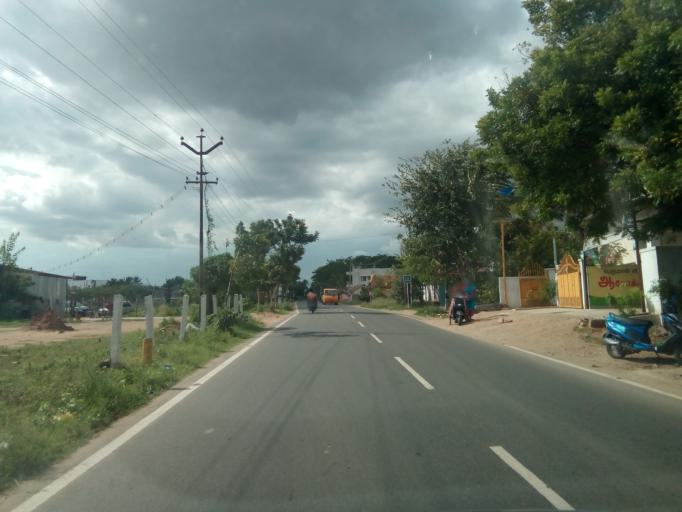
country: IN
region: Tamil Nadu
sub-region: Coimbatore
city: Irugur
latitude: 11.0841
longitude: 77.0350
